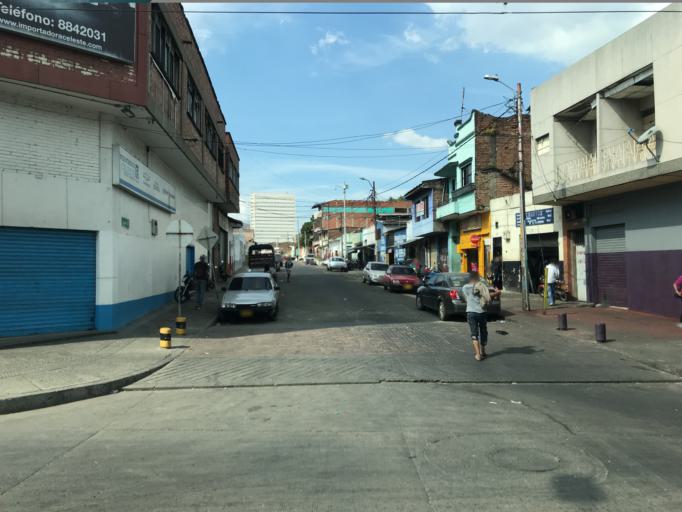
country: CO
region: Valle del Cauca
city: Cali
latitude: 3.4428
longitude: -76.5294
